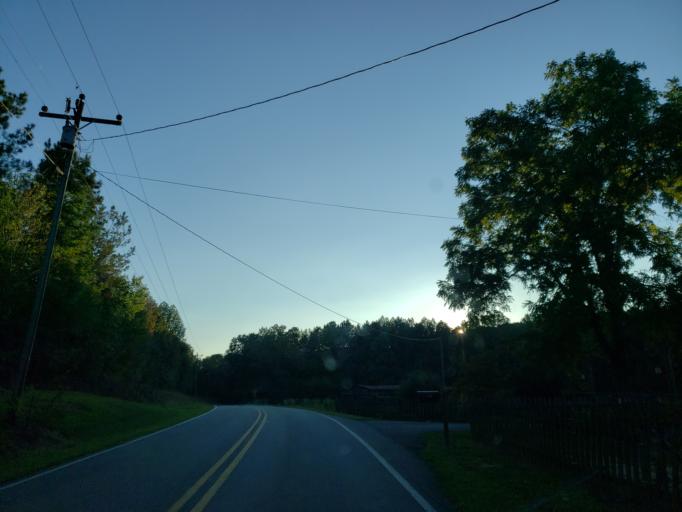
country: US
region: Georgia
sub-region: Bartow County
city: Rydal
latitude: 34.3574
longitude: -84.5774
